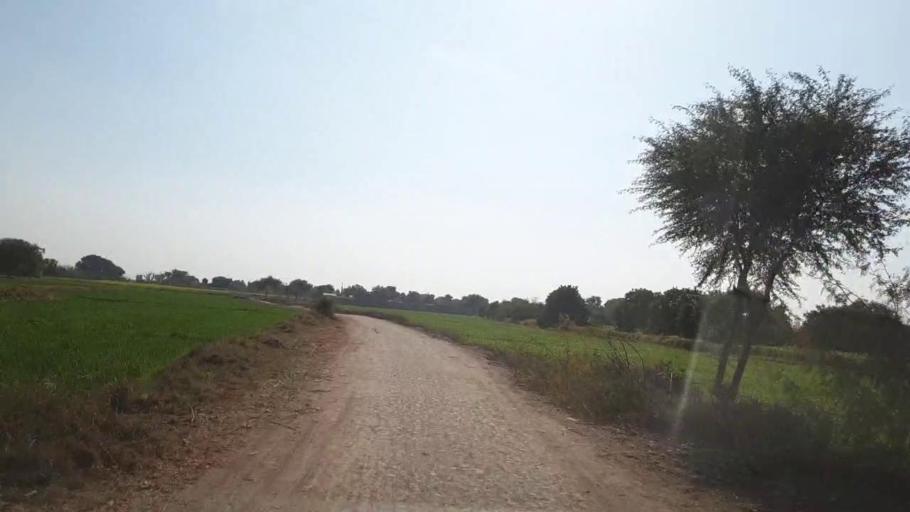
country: PK
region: Sindh
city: Tando Jam
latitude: 25.4988
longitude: 68.4999
